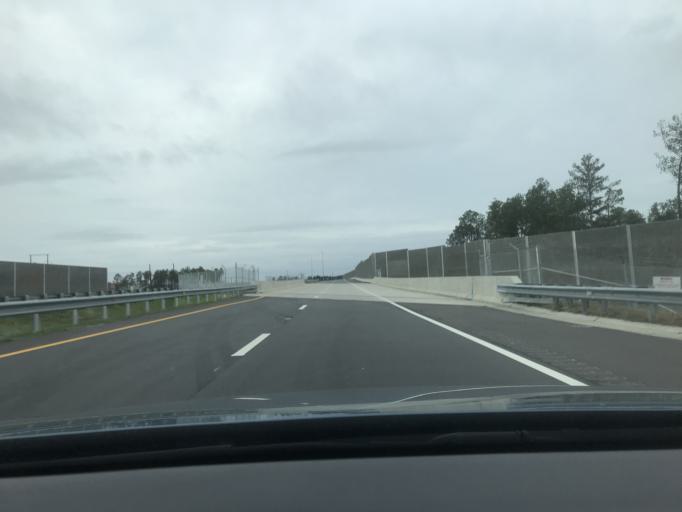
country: US
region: North Carolina
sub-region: Cumberland County
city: Fort Bragg
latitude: 35.1073
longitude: -79.0032
